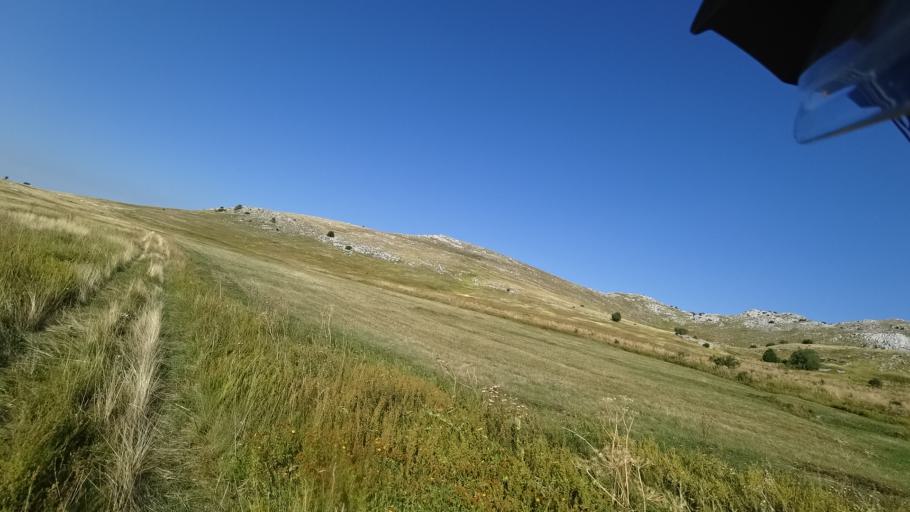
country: HR
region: Sibensko-Kniniska
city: Knin
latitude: 44.2026
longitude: 16.1371
